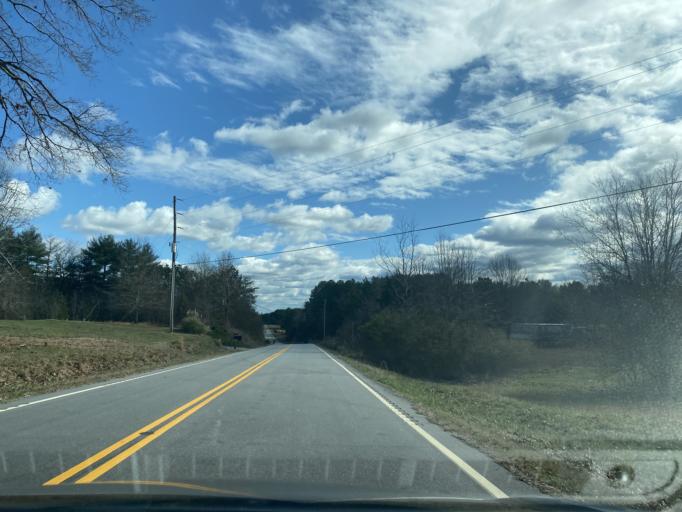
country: US
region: South Carolina
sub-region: Spartanburg County
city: Cowpens
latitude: 35.0966
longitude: -81.7522
